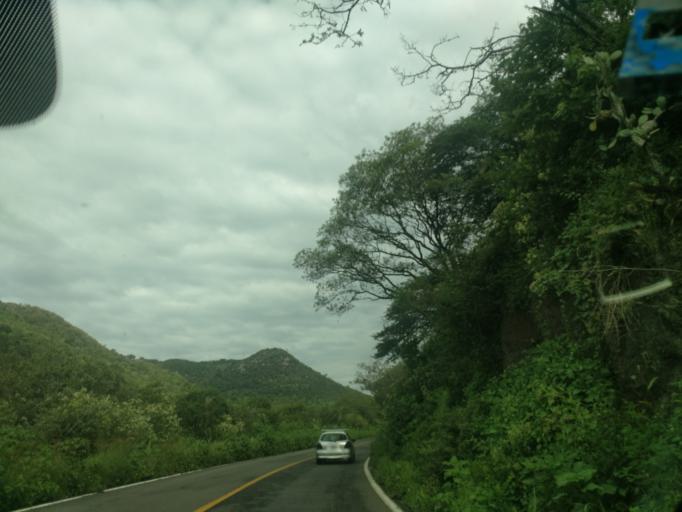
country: MX
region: Jalisco
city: Ameca
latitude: 20.5327
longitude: -104.2662
